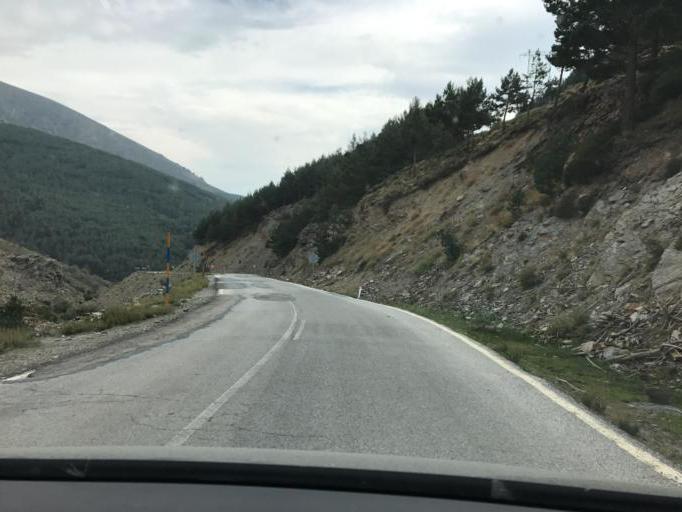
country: ES
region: Andalusia
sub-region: Provincia de Granada
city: Ferreira
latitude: 37.1027
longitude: -3.0261
